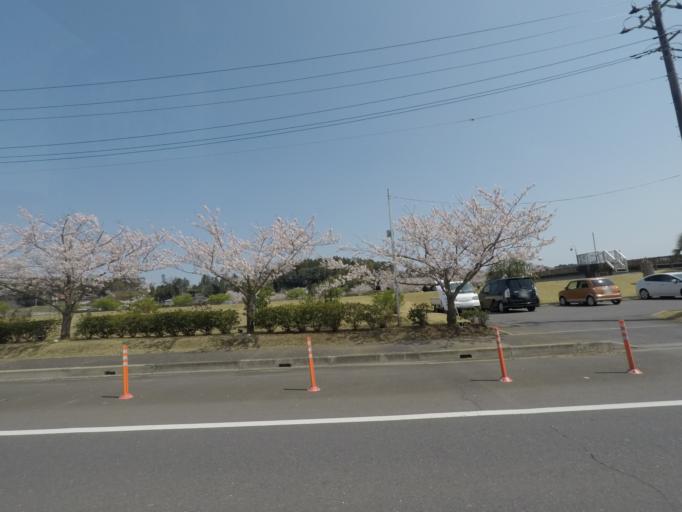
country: JP
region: Chiba
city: Yokaichiba
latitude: 35.7370
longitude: 140.4748
